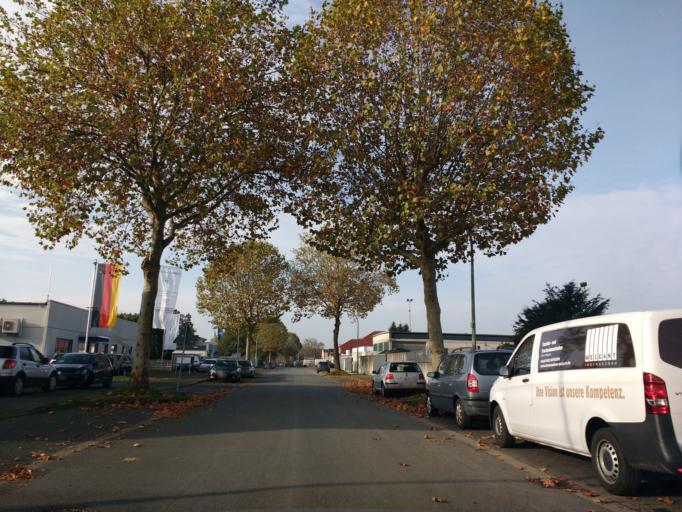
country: DE
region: North Rhine-Westphalia
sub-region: Regierungsbezirk Detmold
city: Paderborn
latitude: 51.7480
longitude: 8.7608
